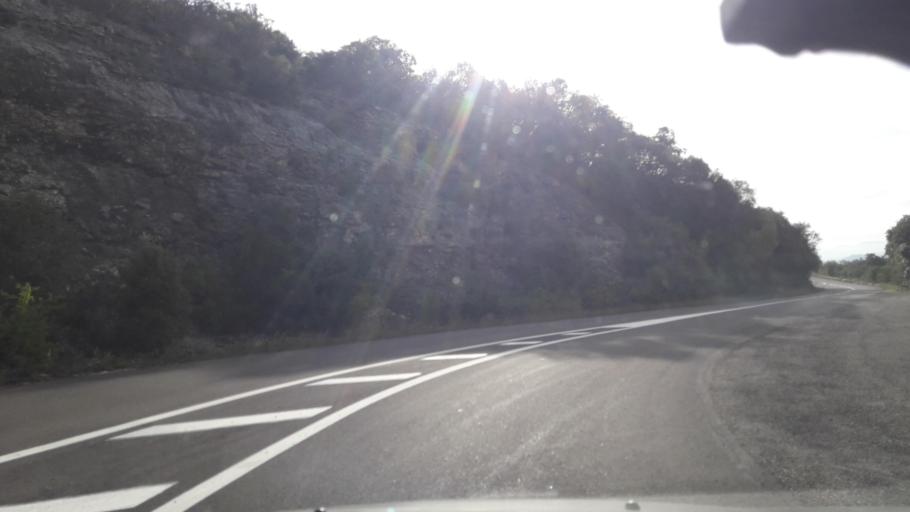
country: FR
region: Languedoc-Roussillon
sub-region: Departement du Gard
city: Saint-Julien-de-Peyrolas
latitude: 44.3318
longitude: 4.5413
